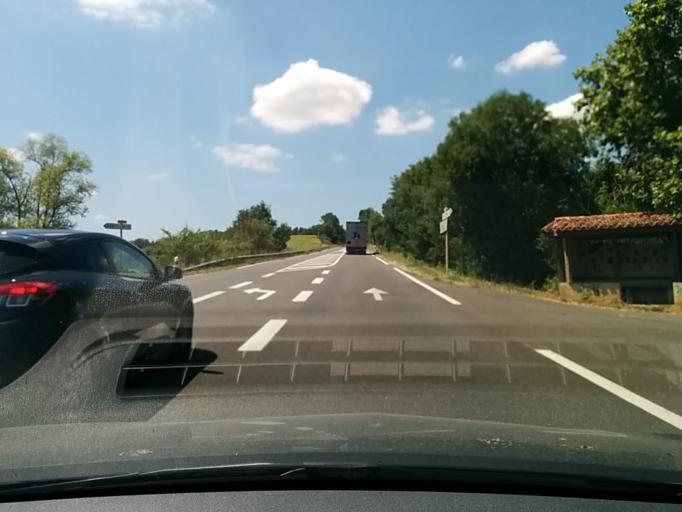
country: FR
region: Midi-Pyrenees
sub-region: Departement du Gers
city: Vic-Fezensac
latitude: 43.7527
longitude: 0.2609
